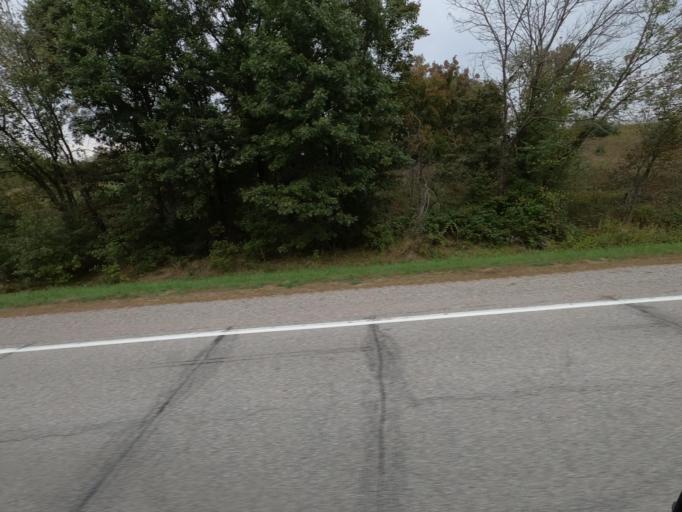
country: US
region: Iowa
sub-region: Van Buren County
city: Keosauqua
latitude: 40.8352
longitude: -91.9570
